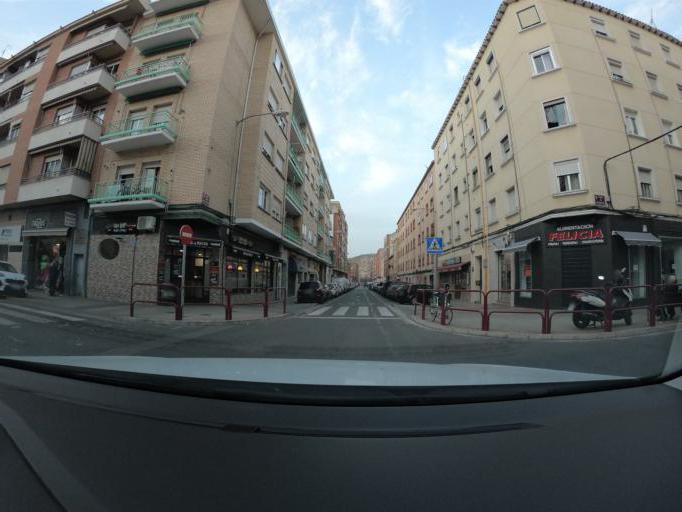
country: ES
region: La Rioja
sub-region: Provincia de La Rioja
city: Logrono
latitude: 42.4650
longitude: -2.4319
